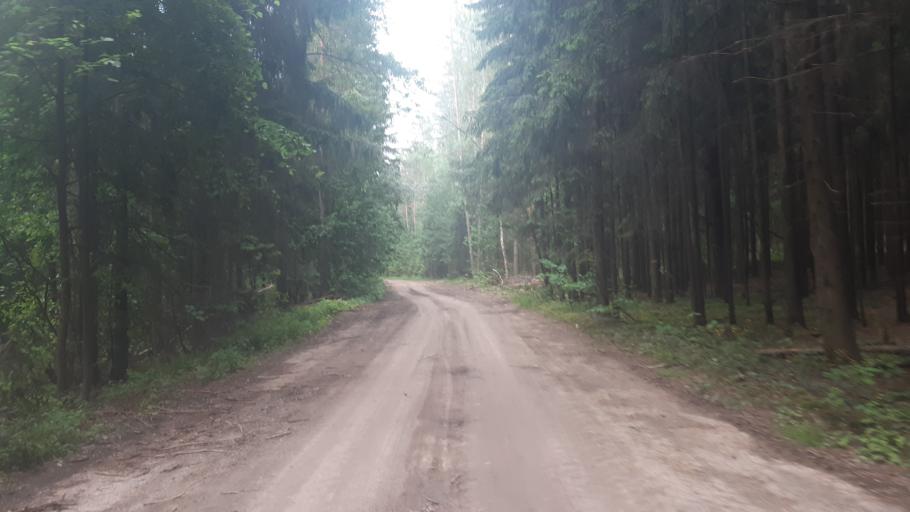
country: BY
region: Minsk
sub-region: Smalyavitski Rayon
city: Oktjabr'skij
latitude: 54.1361
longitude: 28.2267
